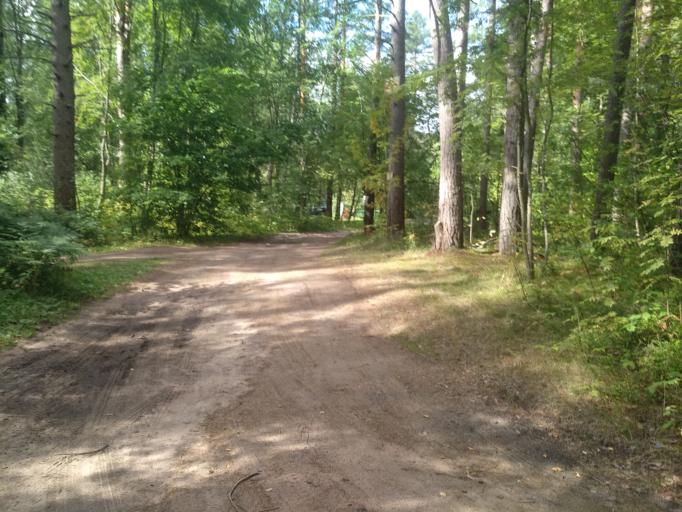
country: RU
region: Leningrad
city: Sapernoye
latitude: 60.6773
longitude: 29.9197
